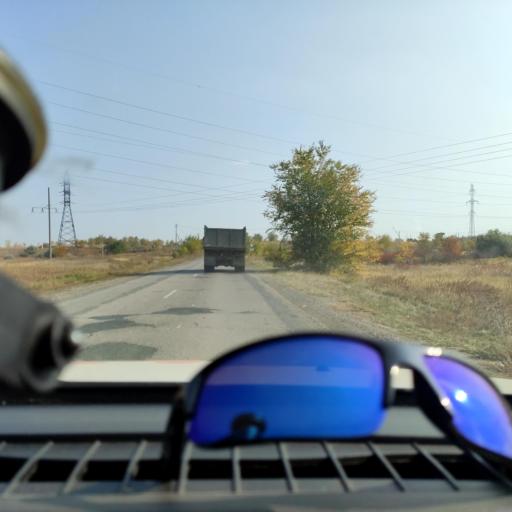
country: RU
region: Samara
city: Chapayevsk
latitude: 53.0003
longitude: 49.7637
